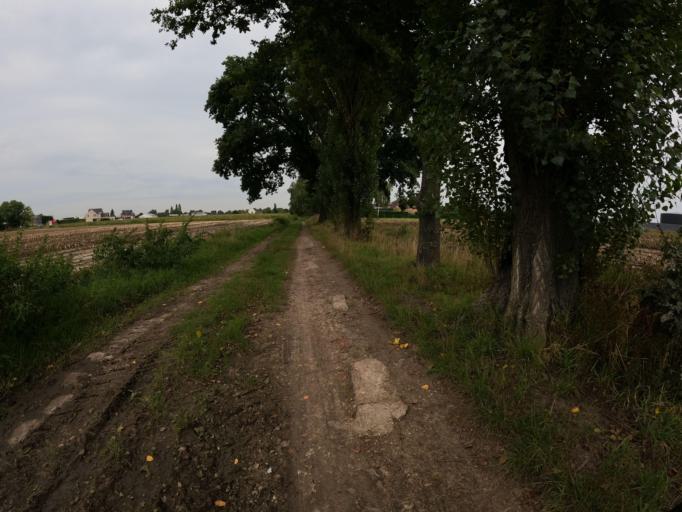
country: BE
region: Flanders
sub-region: Provincie Antwerpen
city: Wommelgem
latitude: 51.1899
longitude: 4.5108
